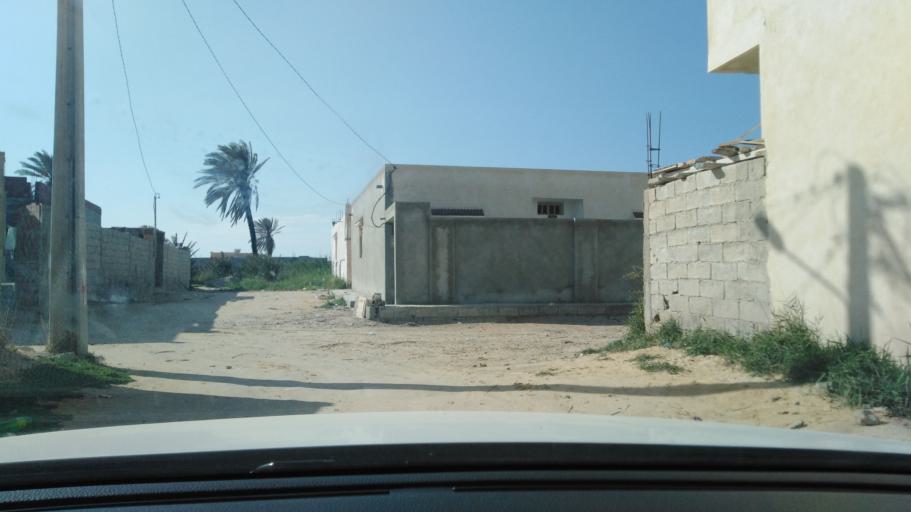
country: TN
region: Qabis
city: Gabes
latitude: 33.9435
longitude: 10.0758
